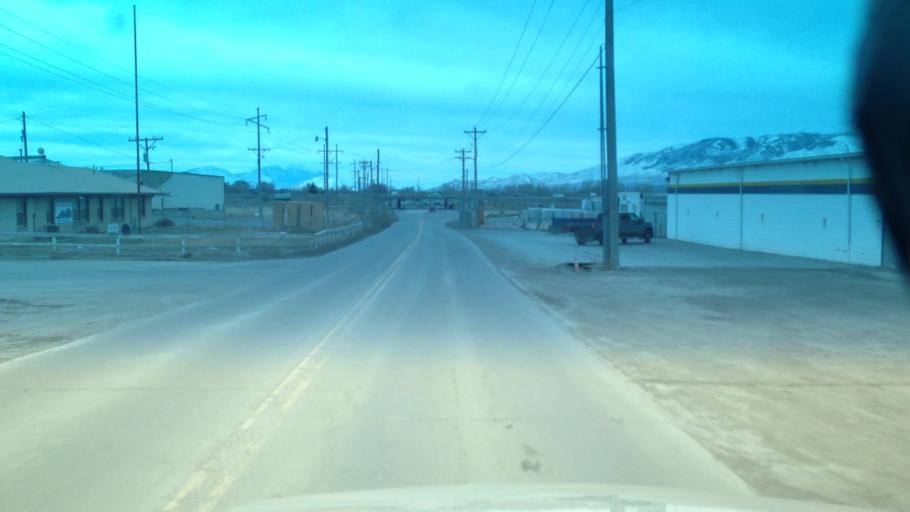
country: US
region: Utah
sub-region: Utah County
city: Lehi
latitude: 40.4177
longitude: -111.8688
